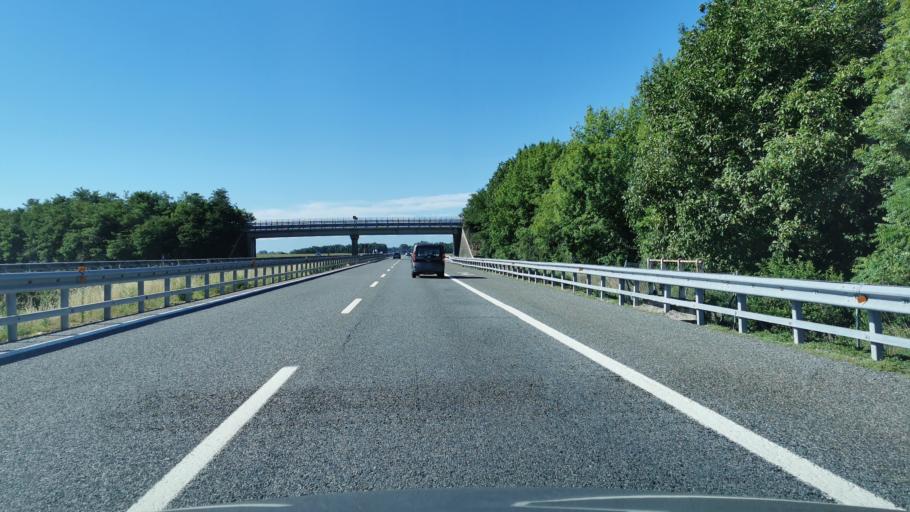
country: IT
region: Piedmont
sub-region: Provincia di Cuneo
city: Caramagna Piemonte
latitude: 44.7678
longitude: 7.7511
